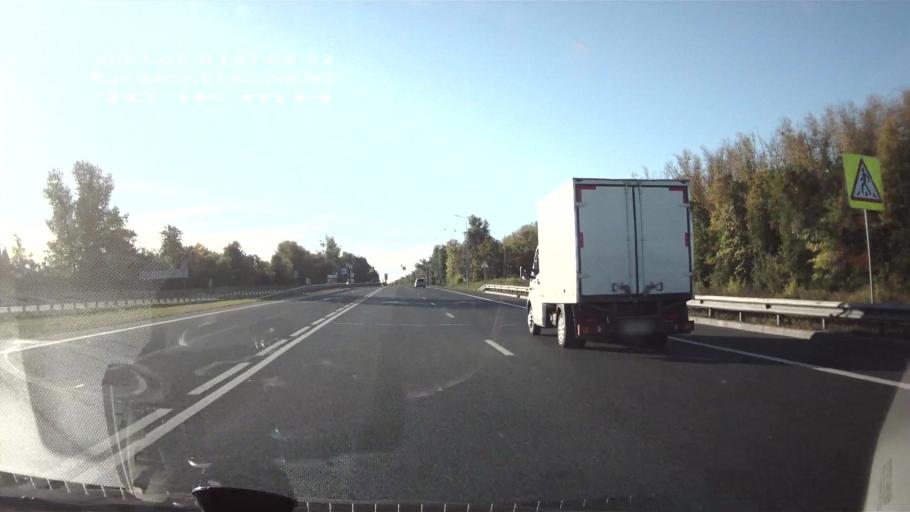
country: RU
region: Chuvashia
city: Tsivil'sk
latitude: 55.9239
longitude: 47.3972
